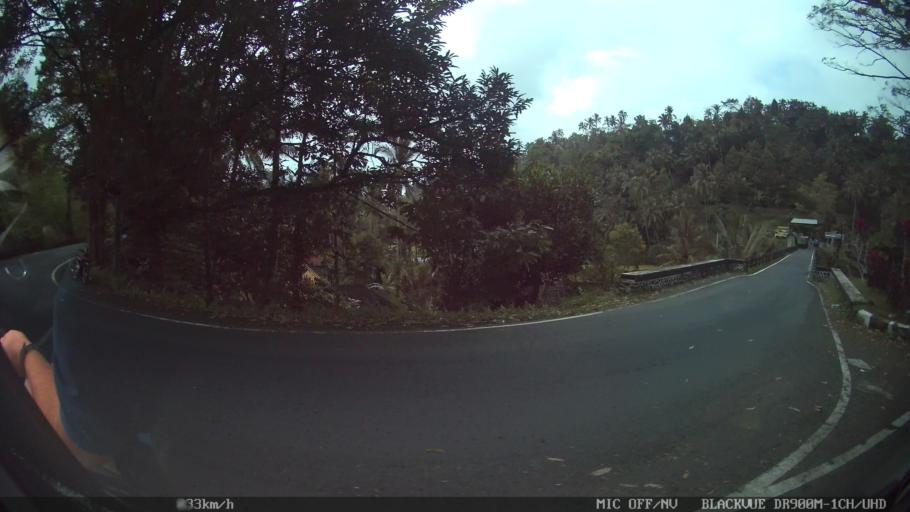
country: ID
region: Bali
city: Banjar Geriana Kangin
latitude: -8.4241
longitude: 115.4338
